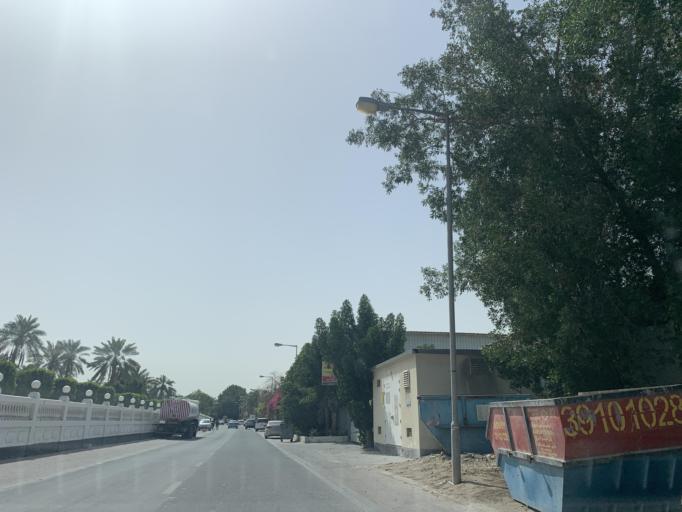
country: BH
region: Manama
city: Jidd Hafs
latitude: 26.2223
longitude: 50.5584
